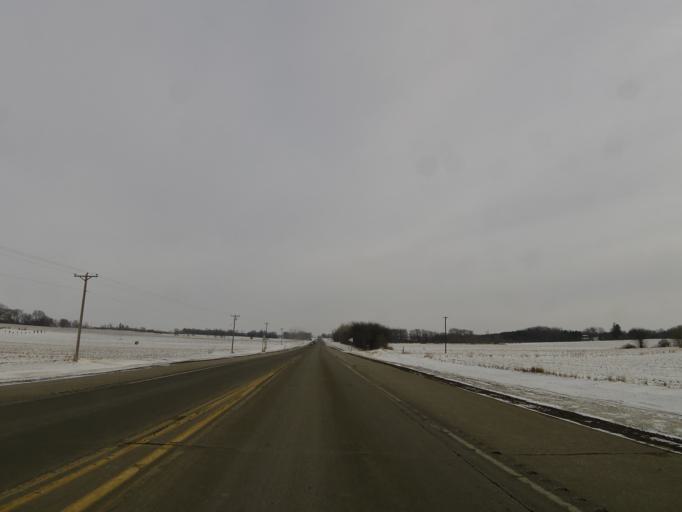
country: US
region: Minnesota
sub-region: McLeod County
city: Glencoe
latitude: 44.9068
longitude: -94.1821
